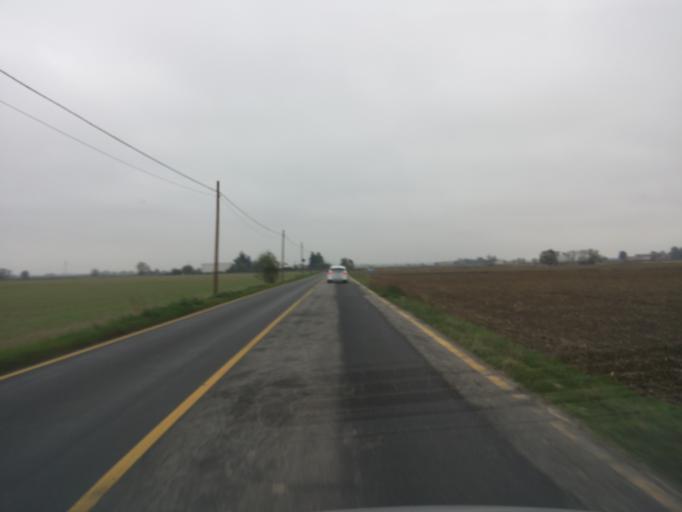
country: IT
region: Piedmont
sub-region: Provincia di Novara
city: Lumellogno
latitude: 45.4000
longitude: 8.5448
